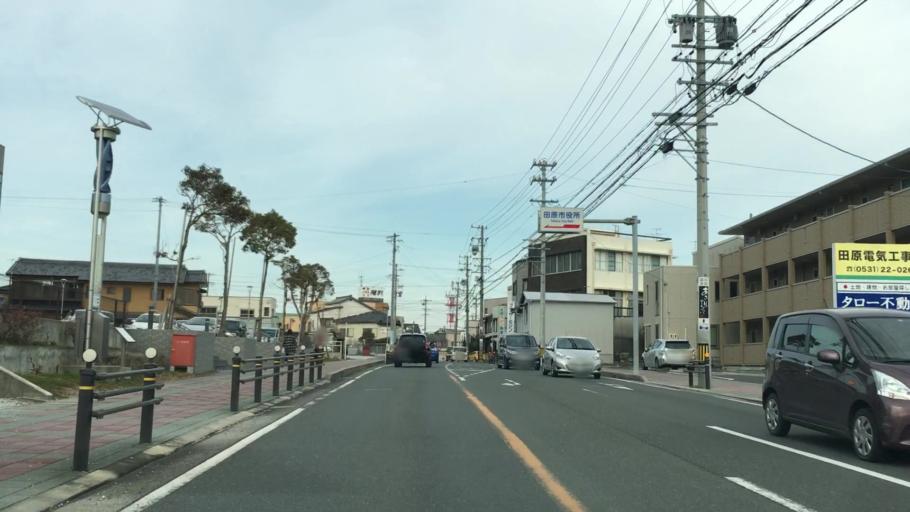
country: JP
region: Aichi
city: Tahara
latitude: 34.6683
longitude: 137.2641
